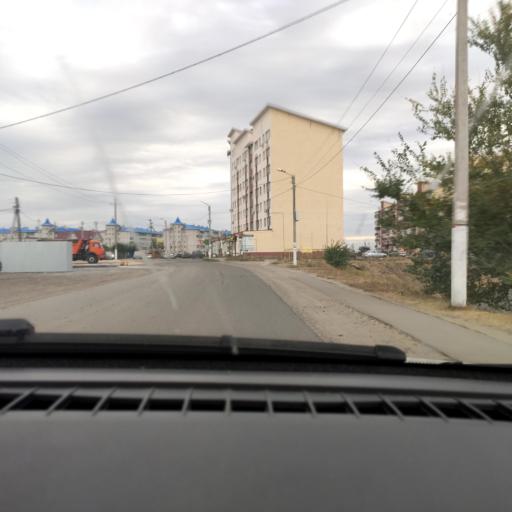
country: RU
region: Voronezj
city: Novaya Usman'
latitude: 51.6088
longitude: 39.3876
